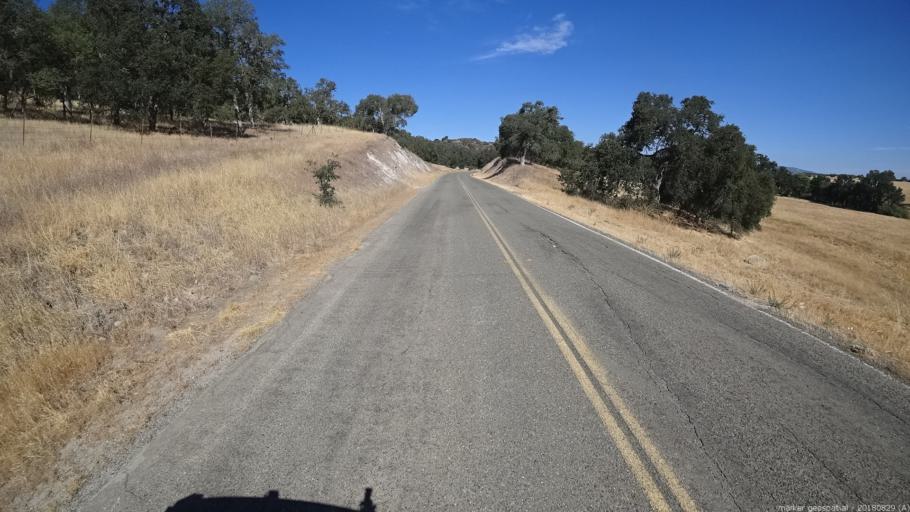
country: US
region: California
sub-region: San Luis Obispo County
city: Lake Nacimiento
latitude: 35.8126
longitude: -121.0052
